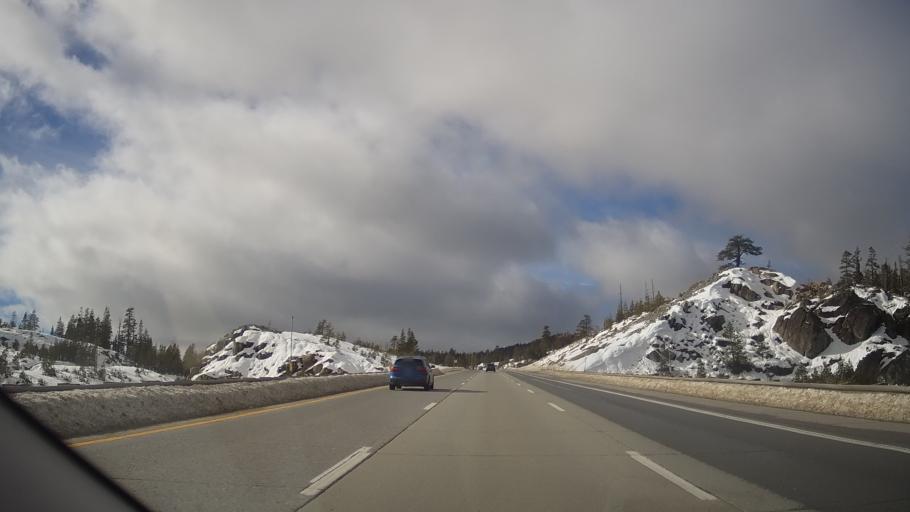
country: US
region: California
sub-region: Nevada County
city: Truckee
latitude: 39.3433
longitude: -120.3285
